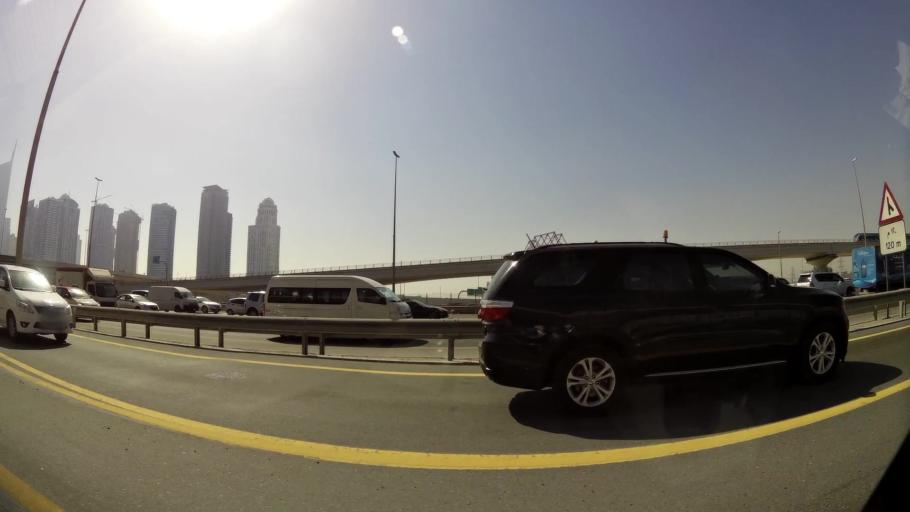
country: AE
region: Dubai
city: Dubai
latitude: 25.0632
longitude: 55.1308
